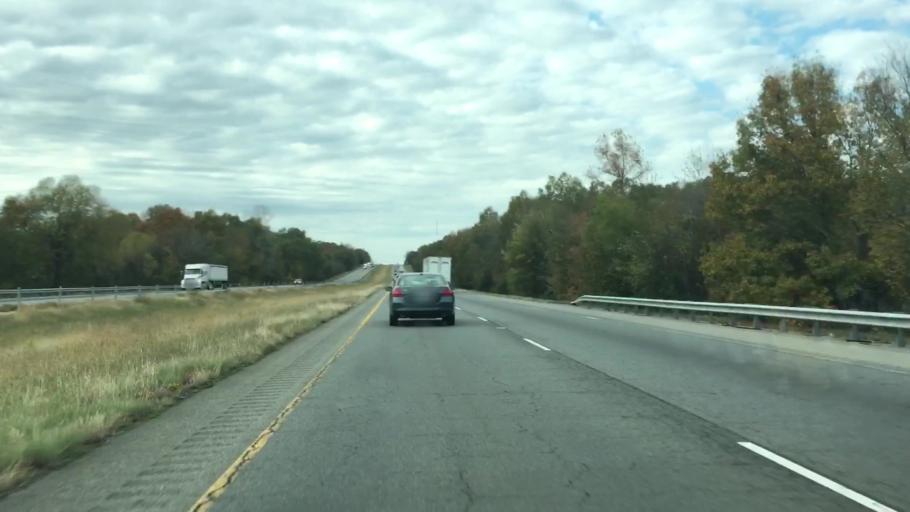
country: US
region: Arkansas
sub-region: Faulkner County
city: Conway
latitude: 35.1395
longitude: -92.5246
